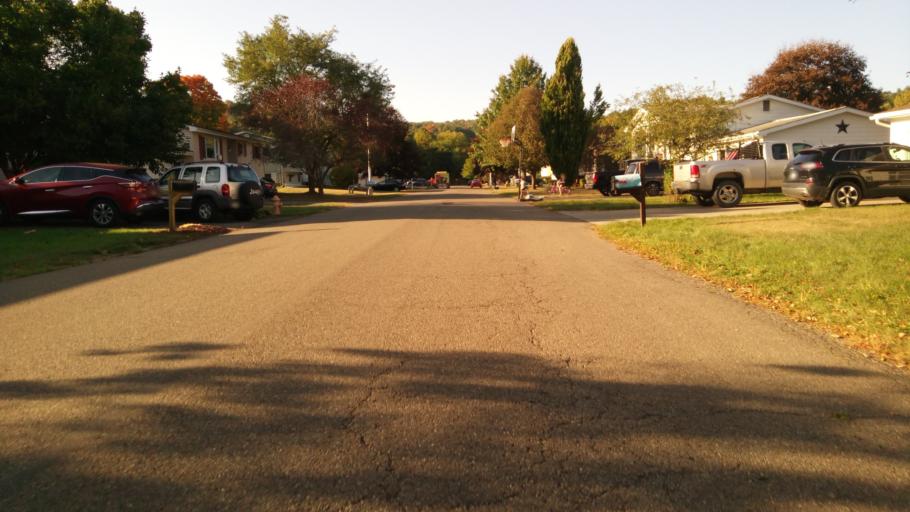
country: US
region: New York
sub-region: Chemung County
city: Southport
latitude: 42.0545
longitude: -76.8351
